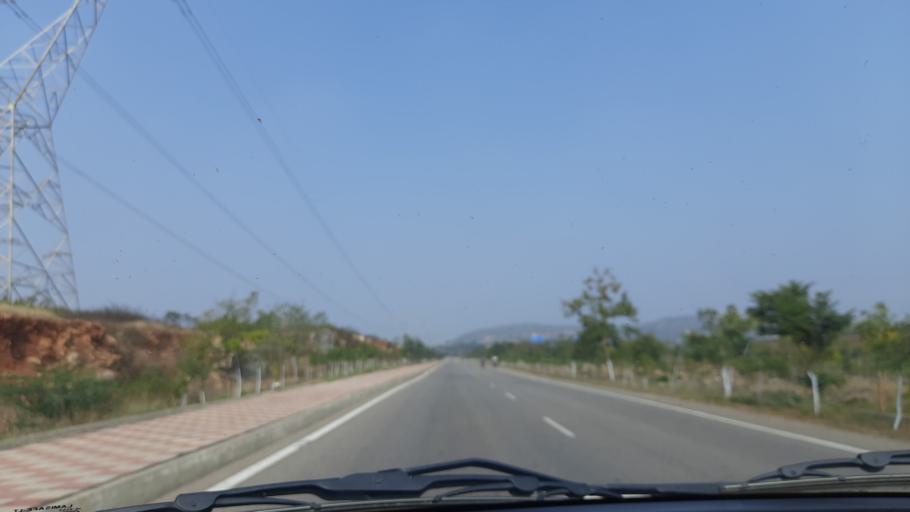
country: IN
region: Telangana
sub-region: Rangareddi
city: Lal Bahadur Nagar
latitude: 17.3086
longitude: 78.6553
